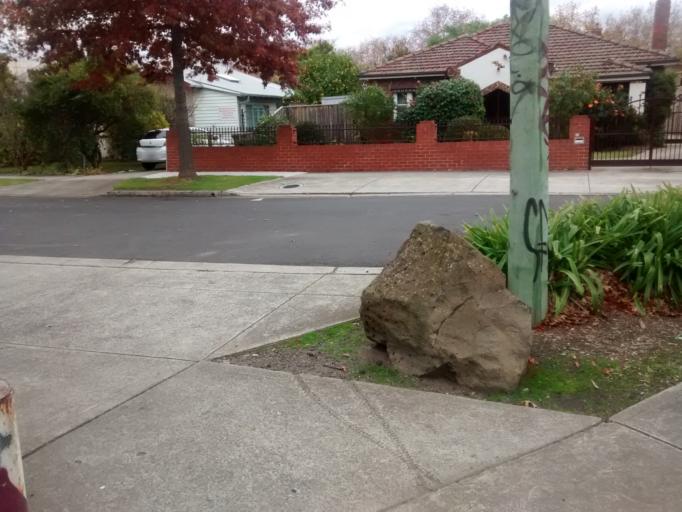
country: AU
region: Victoria
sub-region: Darebin
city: Fairfield
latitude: -37.7798
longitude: 145.0226
